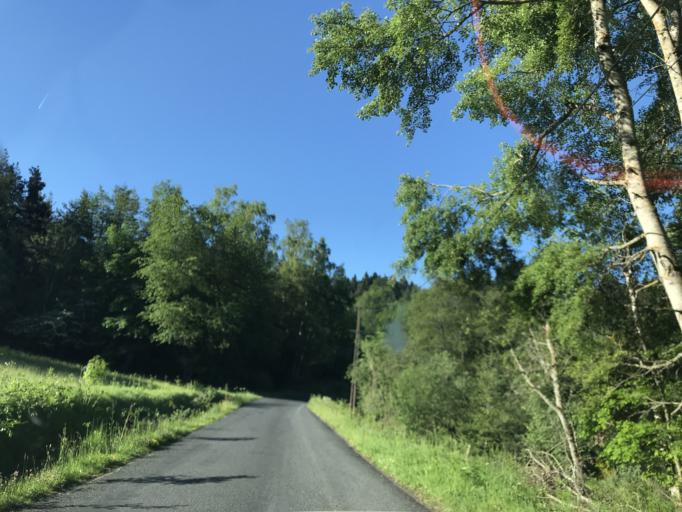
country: FR
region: Auvergne
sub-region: Departement du Puy-de-Dome
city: Job
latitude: 45.6992
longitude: 3.6931
